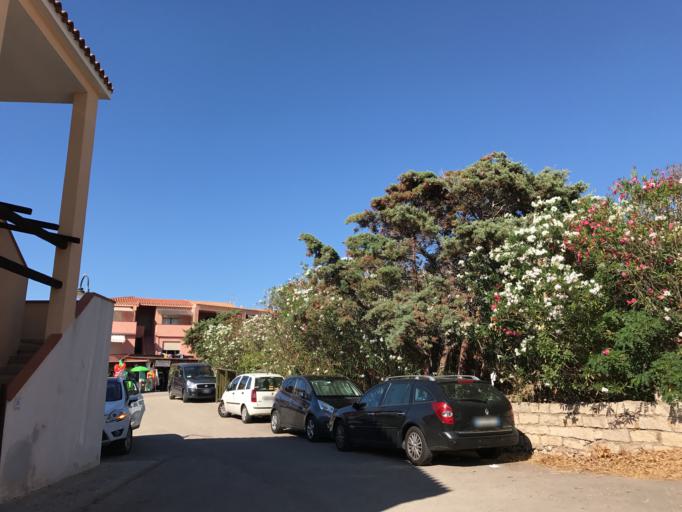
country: IT
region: Sardinia
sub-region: Provincia di Olbia-Tempio
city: Trinita d'Agultu
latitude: 41.0125
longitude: 8.8753
